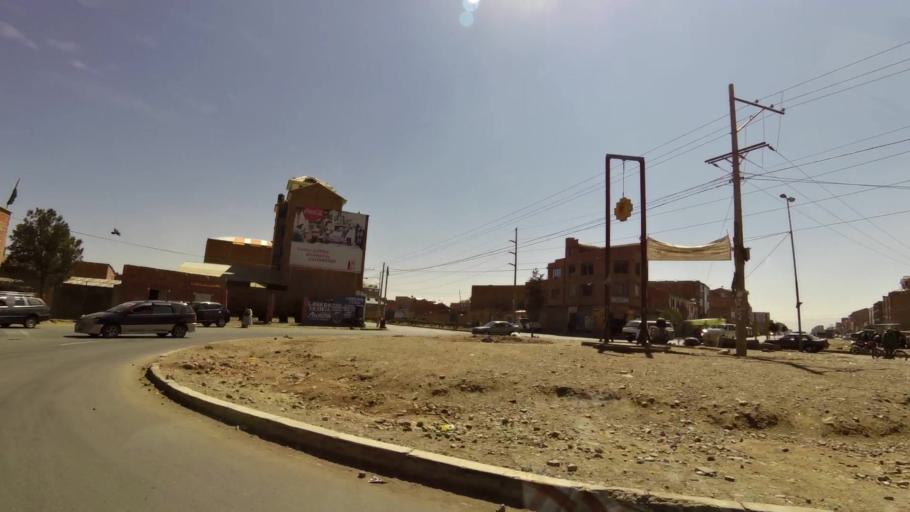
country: BO
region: La Paz
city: La Paz
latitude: -16.5422
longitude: -68.1687
